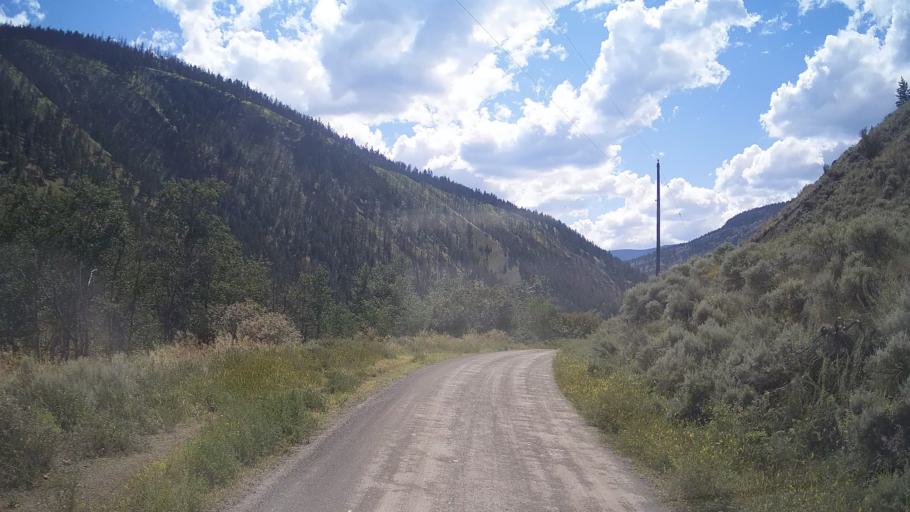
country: CA
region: British Columbia
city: Lillooet
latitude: 51.2211
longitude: -122.0795
